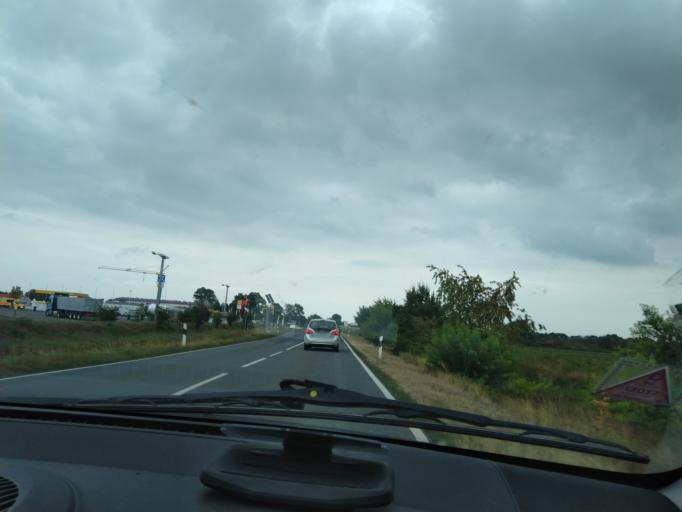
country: DE
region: Lower Saxony
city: Rhede
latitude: 53.0645
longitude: 7.2450
